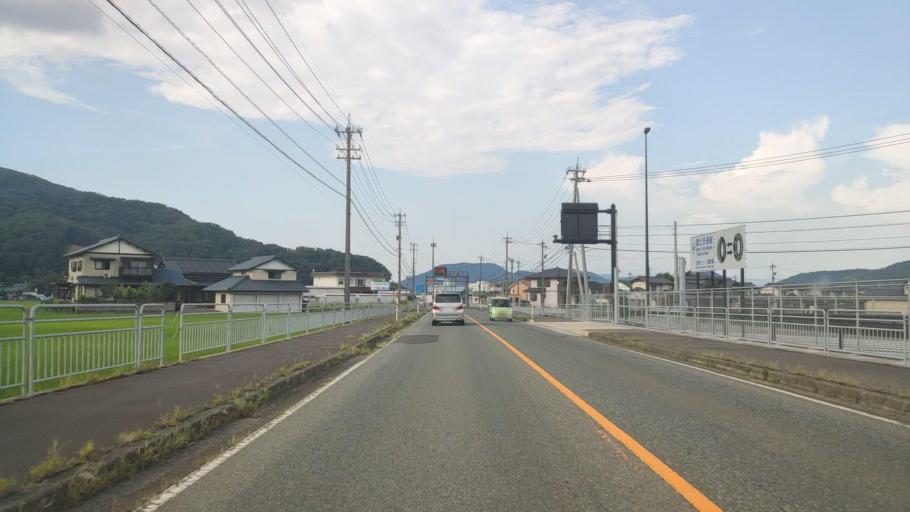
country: JP
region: Fukui
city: Takefu
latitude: 35.8683
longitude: 136.1530
